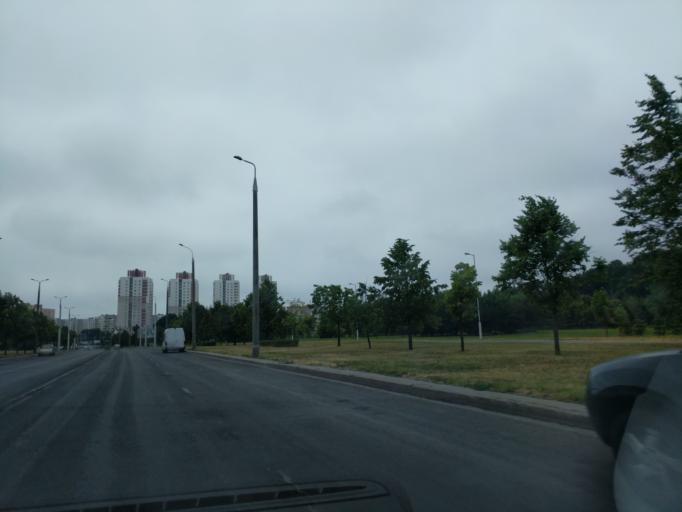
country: BY
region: Minsk
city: Malinovka
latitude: 53.8567
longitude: 27.4537
